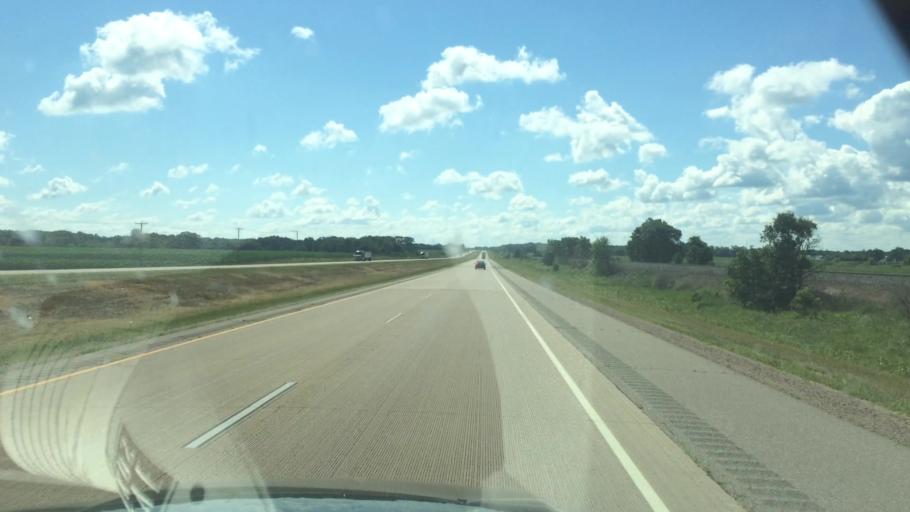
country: US
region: Wisconsin
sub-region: Portage County
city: Amherst
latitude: 44.4924
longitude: -89.3629
